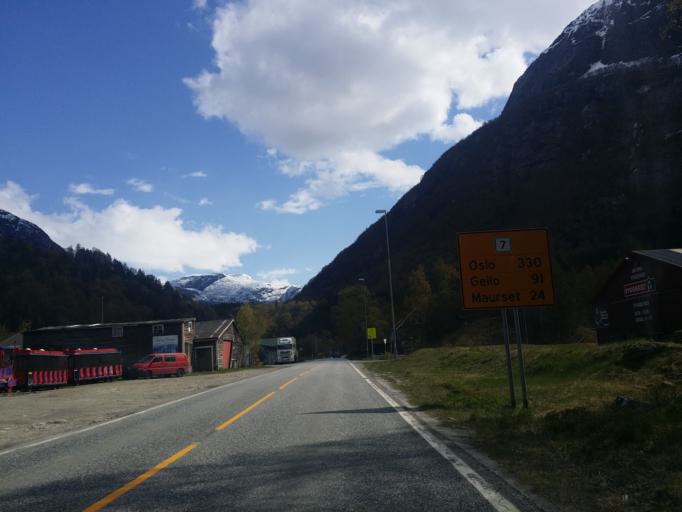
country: NO
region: Hordaland
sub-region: Eidfjord
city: Eidfjord
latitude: 60.4624
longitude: 7.0785
